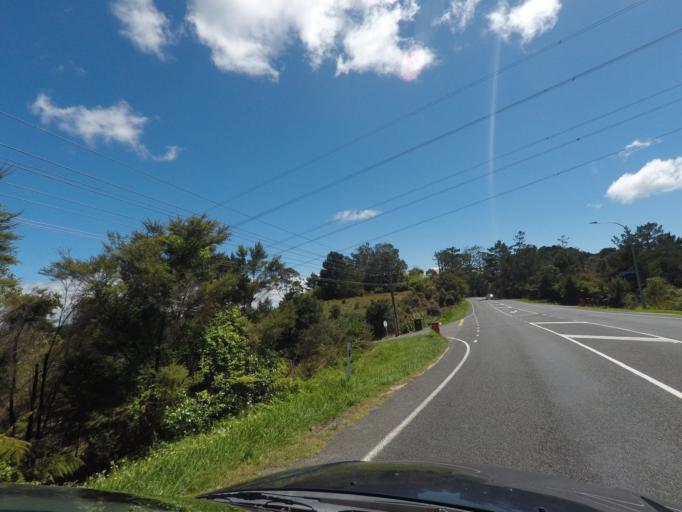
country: NZ
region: Auckland
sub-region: Auckland
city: Rothesay Bay
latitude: -36.7361
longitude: 174.6758
